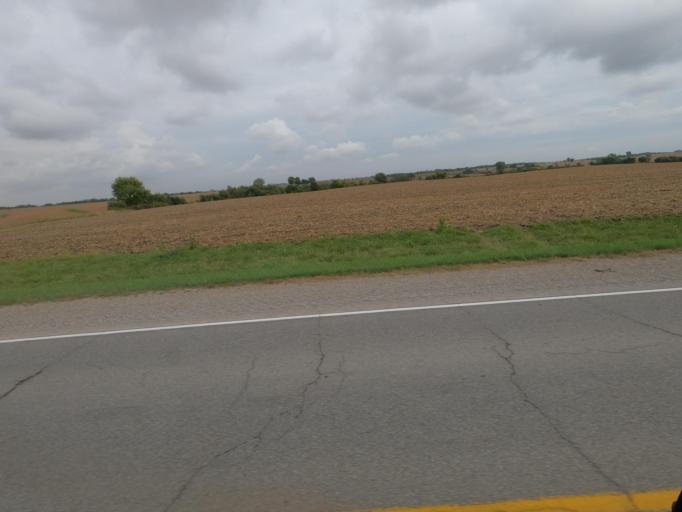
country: US
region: Iowa
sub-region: Wapello County
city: Ottumwa
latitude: 40.9601
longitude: -92.2365
